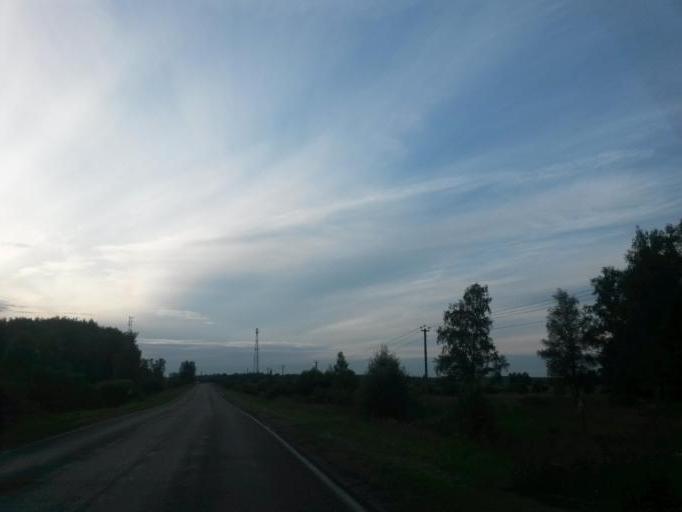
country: RU
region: Moskovskaya
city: Lyubuchany
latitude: 55.2311
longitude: 37.6485
